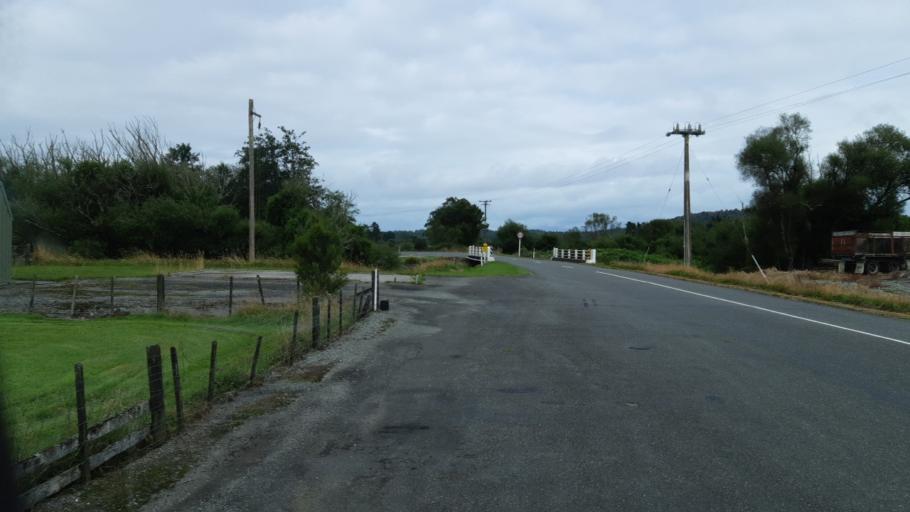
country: NZ
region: West Coast
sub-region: Westland District
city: Hokitika
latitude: -42.8329
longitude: 171.0332
